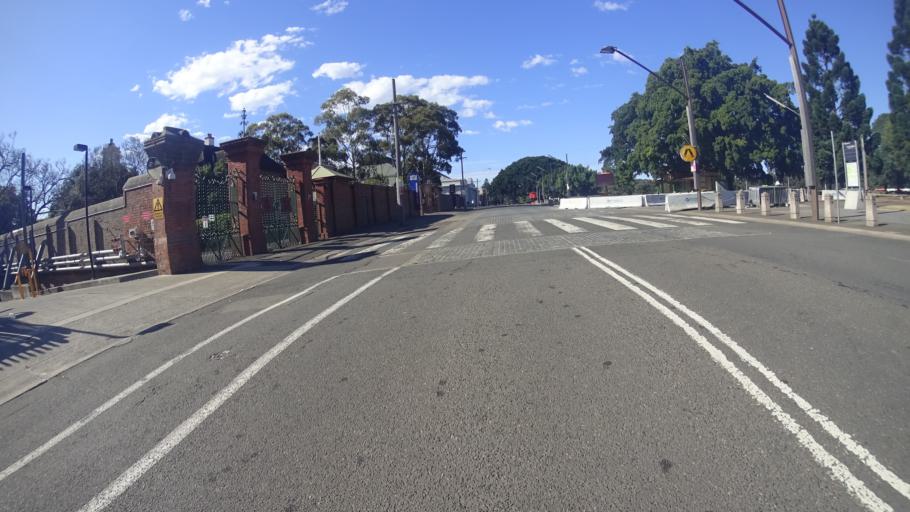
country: AU
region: New South Wales
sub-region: Woollahra
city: Paddington
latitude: -33.8928
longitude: 151.2237
